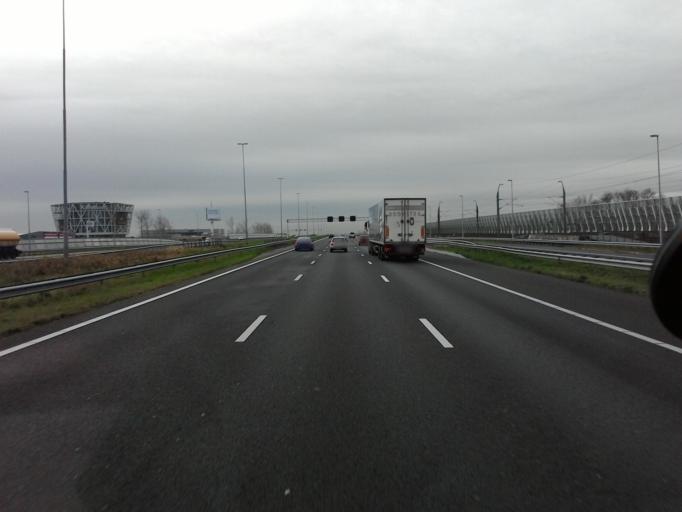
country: NL
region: South Holland
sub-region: Gemeente Kaag en Braassem
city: Oude Wetering
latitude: 52.2026
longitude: 4.6170
